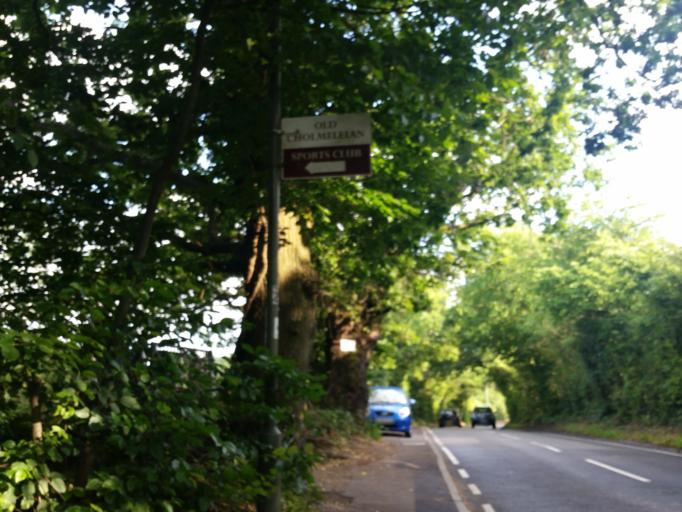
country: GB
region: England
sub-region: Greater London
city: High Barnet
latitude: 51.6335
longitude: -0.2361
